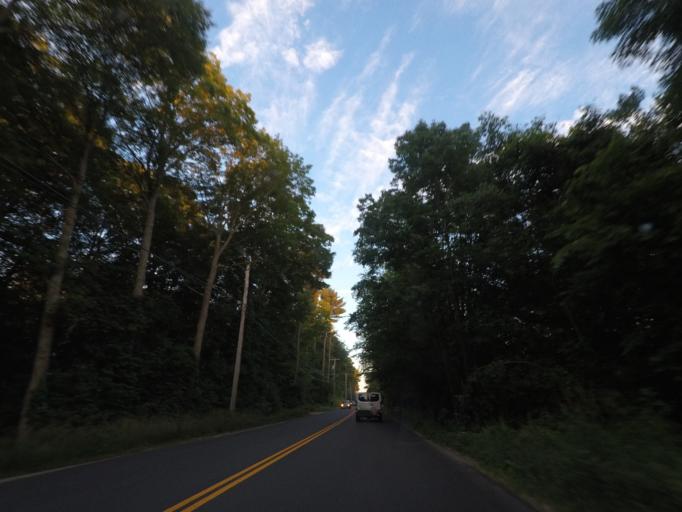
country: US
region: Massachusetts
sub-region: Worcester County
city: Fiskdale
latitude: 42.1390
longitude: -72.1287
